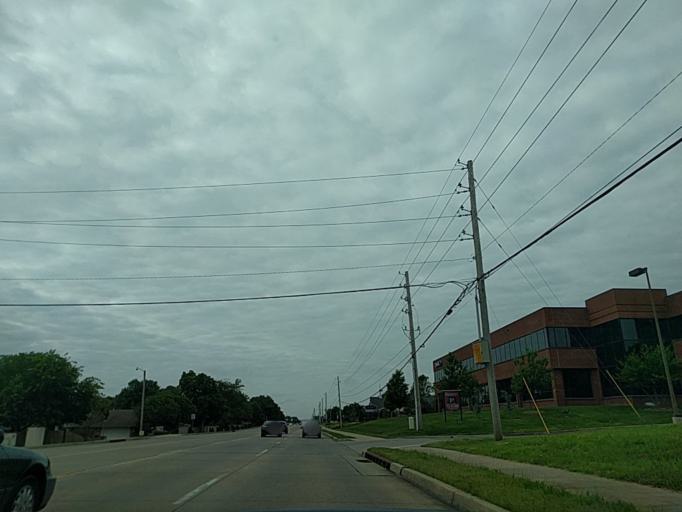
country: US
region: Oklahoma
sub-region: Tulsa County
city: Jenks
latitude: 36.0683
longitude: -95.9044
